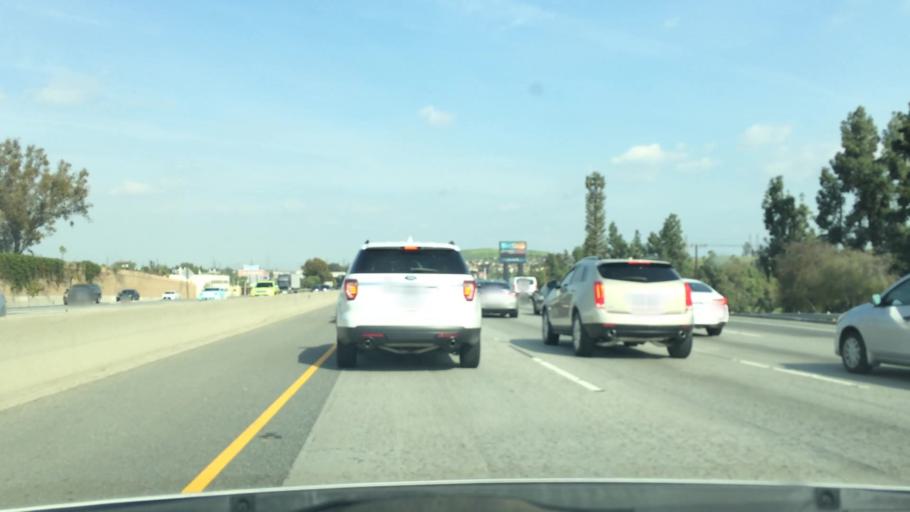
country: US
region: California
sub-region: Los Angeles County
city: Monterey Park
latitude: 34.0336
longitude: -118.1352
